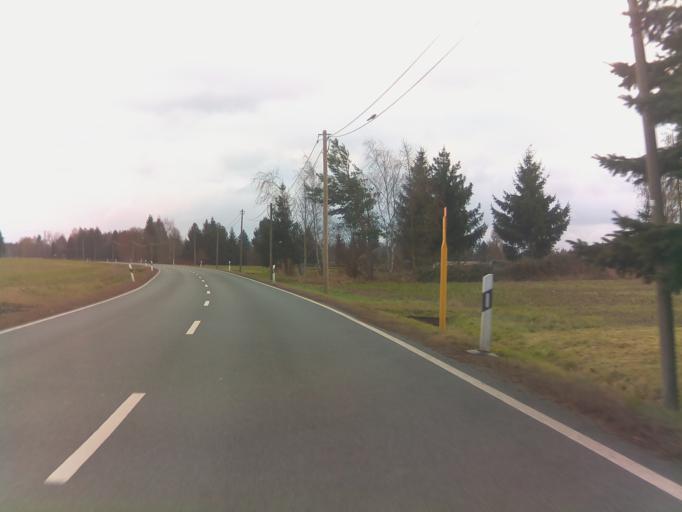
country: DE
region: Thuringia
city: Zeulenroda
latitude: 50.6371
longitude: 11.9882
